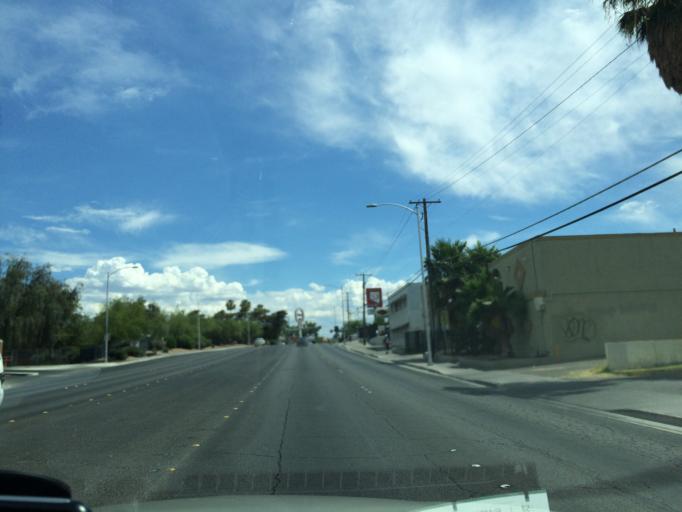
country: US
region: Nevada
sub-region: Clark County
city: Las Vegas
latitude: 36.1836
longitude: -115.1341
